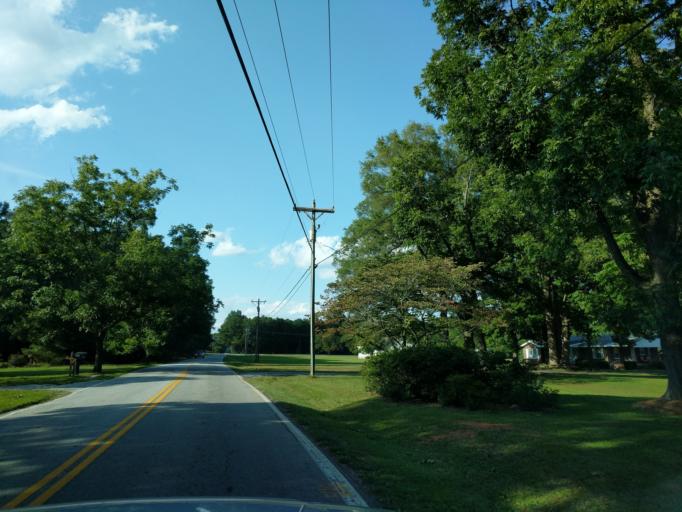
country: US
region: South Carolina
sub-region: Greenville County
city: Fountain Inn
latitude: 34.6784
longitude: -82.2194
